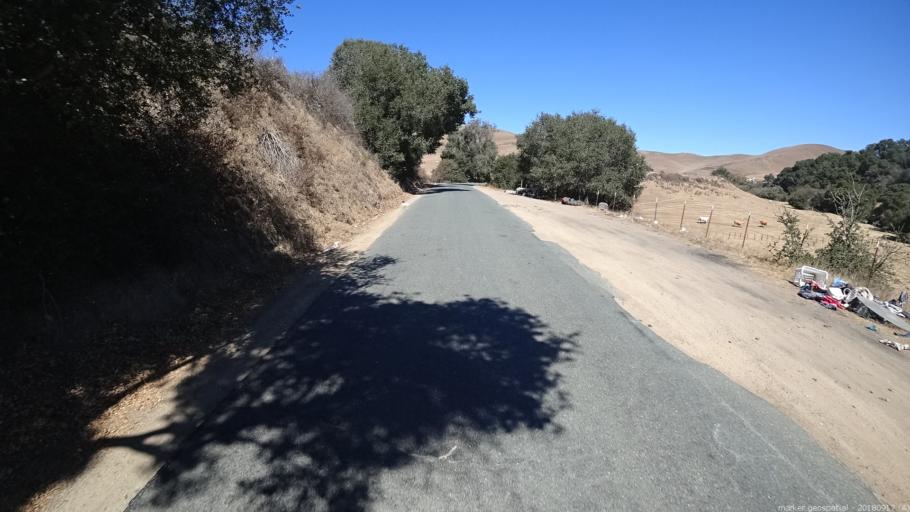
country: US
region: California
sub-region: San Benito County
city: San Juan Bautista
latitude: 36.7977
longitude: -121.5821
